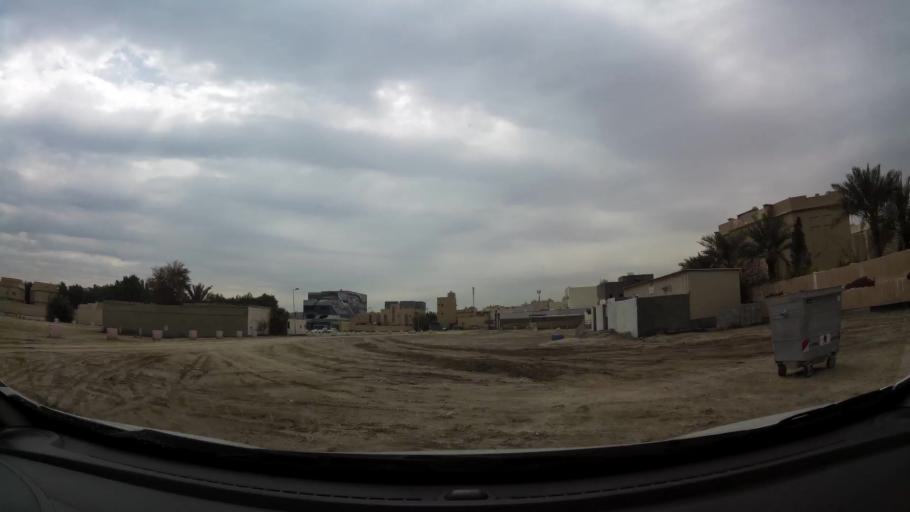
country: BH
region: Manama
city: Manama
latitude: 26.1867
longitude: 50.5829
